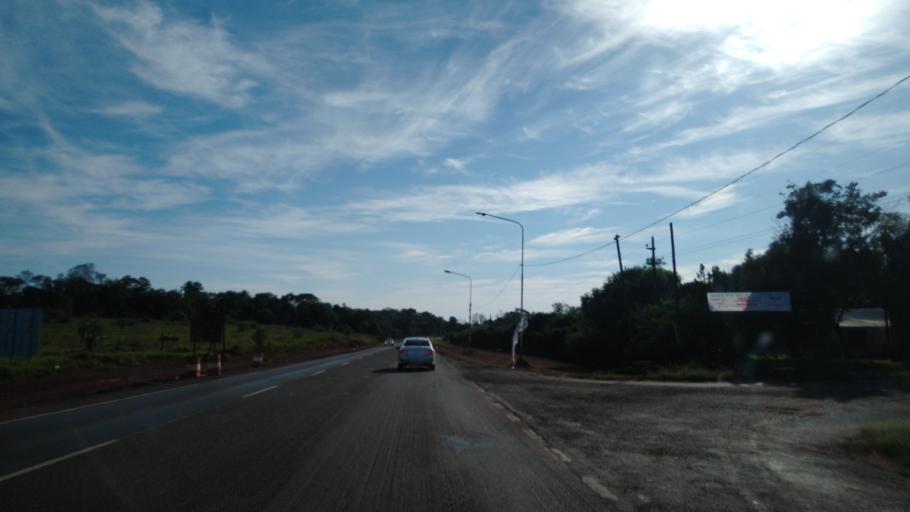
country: AR
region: Misiones
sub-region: Departamento de Candelaria
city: Loreto
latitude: -27.3366
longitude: -55.5444
